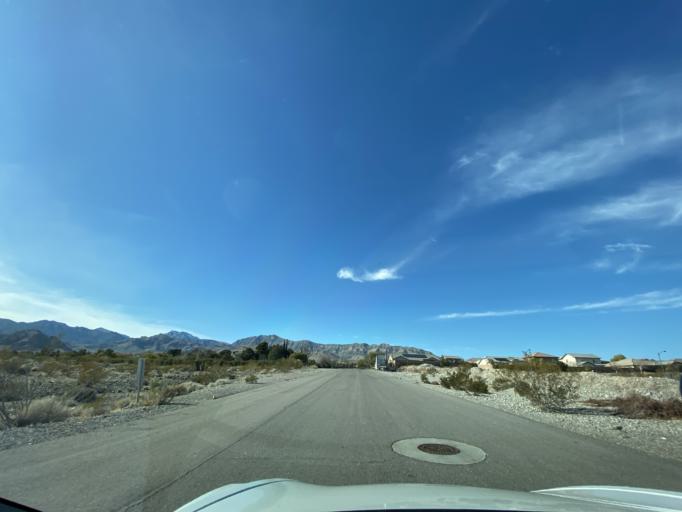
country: US
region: Nevada
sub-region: Clark County
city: Summerlin South
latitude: 36.2847
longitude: -115.3184
